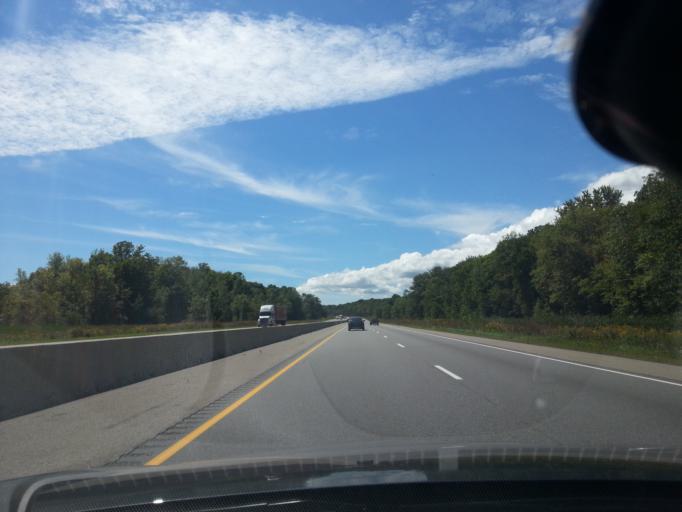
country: CA
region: Ontario
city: Brockville
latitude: 44.5582
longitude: -75.7540
